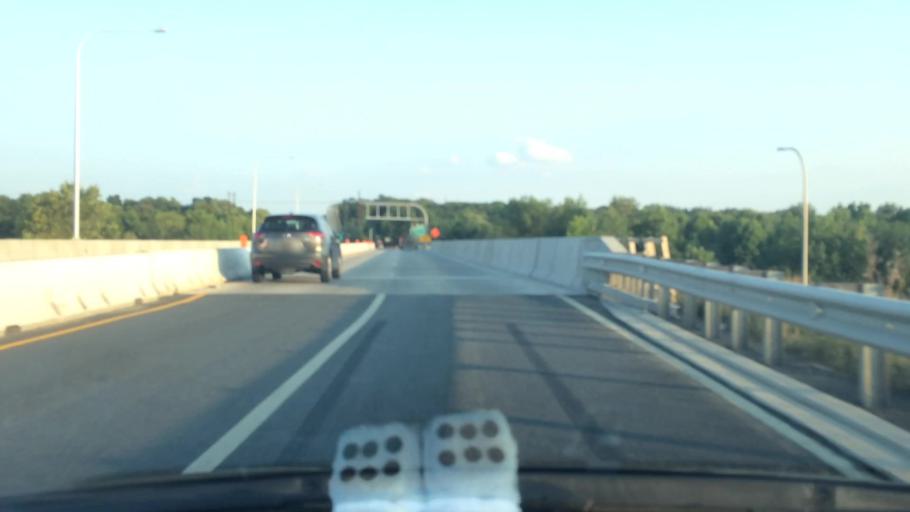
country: US
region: Delaware
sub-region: New Castle County
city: Newport
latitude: 39.7003
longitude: -75.6043
